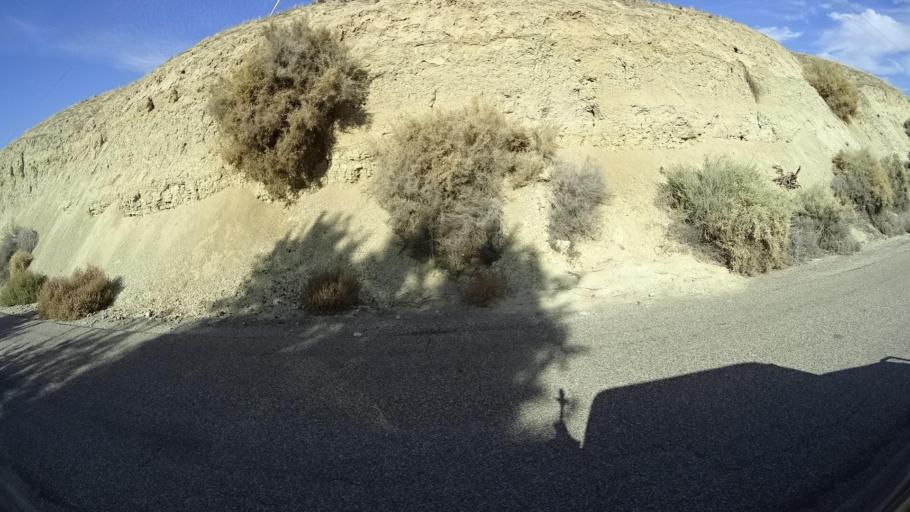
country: US
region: California
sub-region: Kern County
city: Oildale
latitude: 35.5247
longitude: -118.9473
